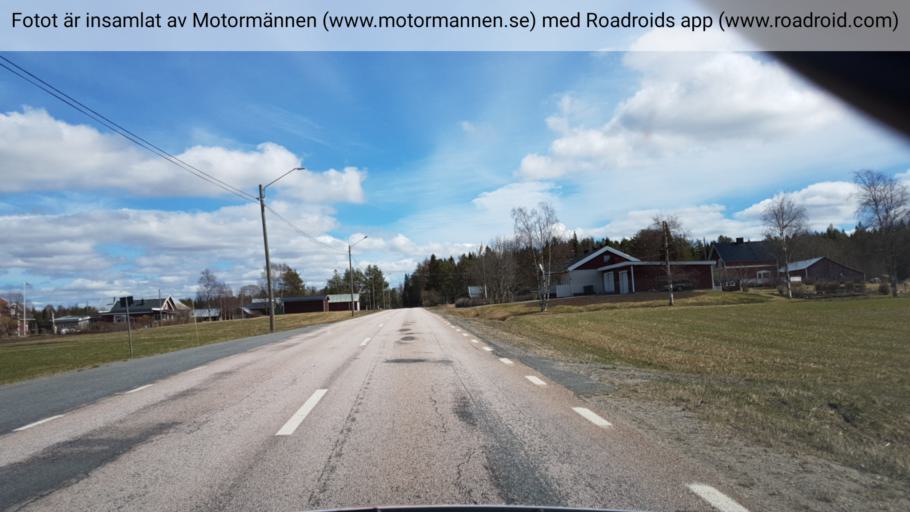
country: SE
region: Vaesternorrland
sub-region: OErnskoeldsviks Kommun
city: Husum
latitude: 63.4787
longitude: 18.9324
